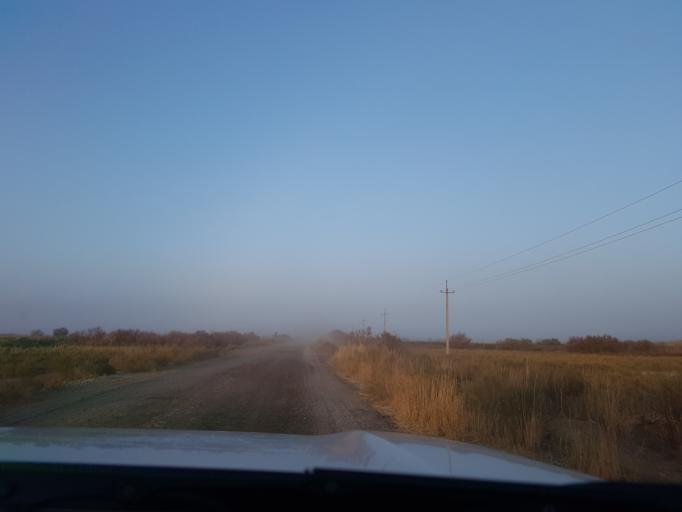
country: TM
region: Dasoguz
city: Koeneuergench
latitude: 41.8446
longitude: 58.5652
